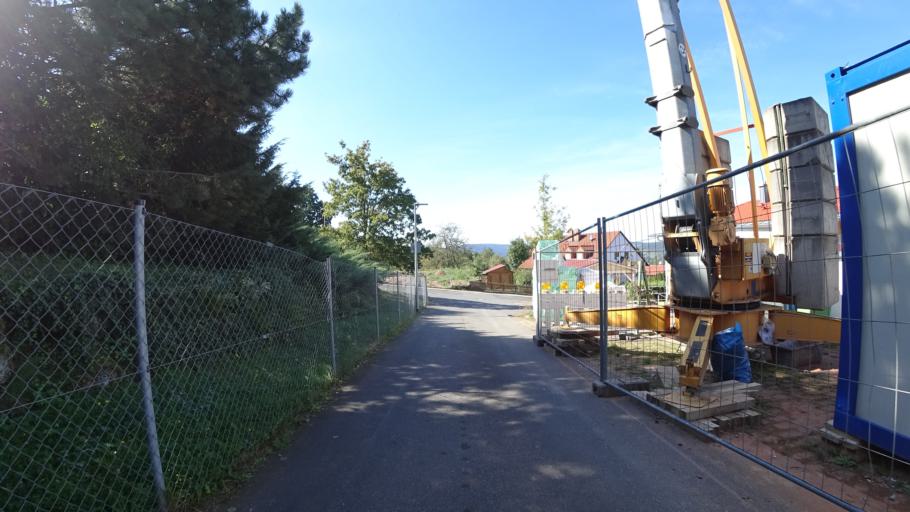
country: DE
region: Bavaria
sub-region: Regierungsbezirk Unterfranken
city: Miltenberg
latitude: 49.6980
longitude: 9.2734
